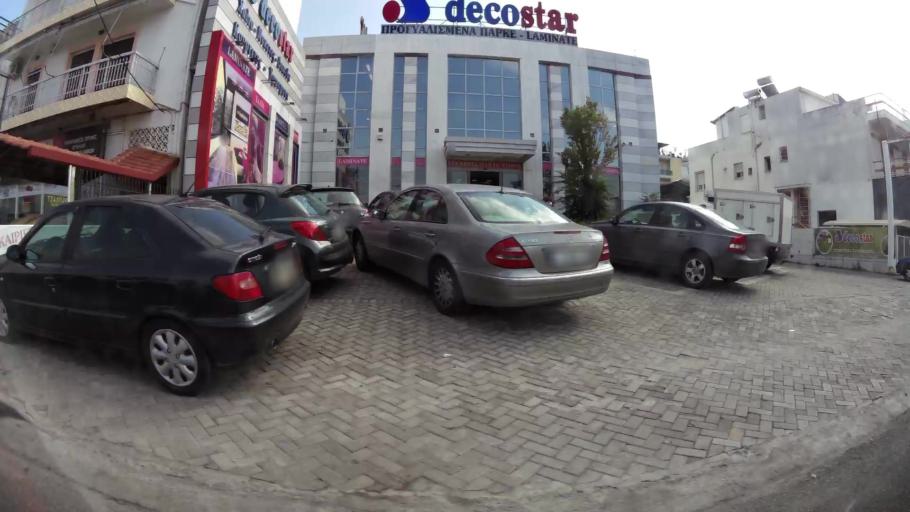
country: GR
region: Attica
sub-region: Nomarchia Dytikis Attikis
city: Zefyri
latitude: 38.0649
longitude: 23.7327
